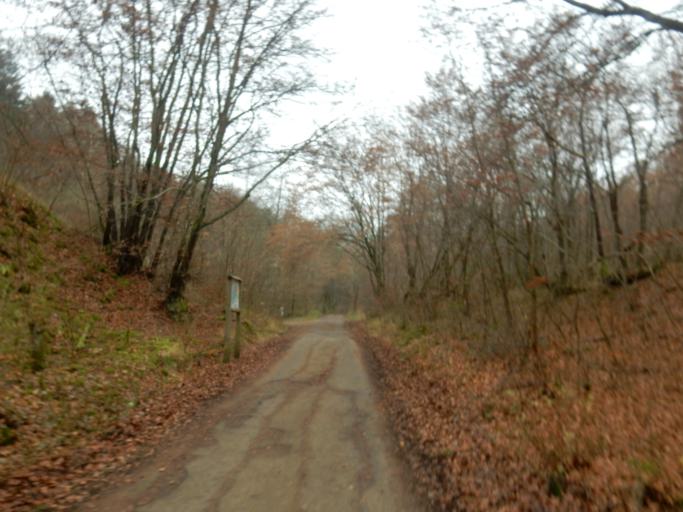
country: LU
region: Luxembourg
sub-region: Canton d'Esch-sur-Alzette
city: Dudelange
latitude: 49.4701
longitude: 6.0708
